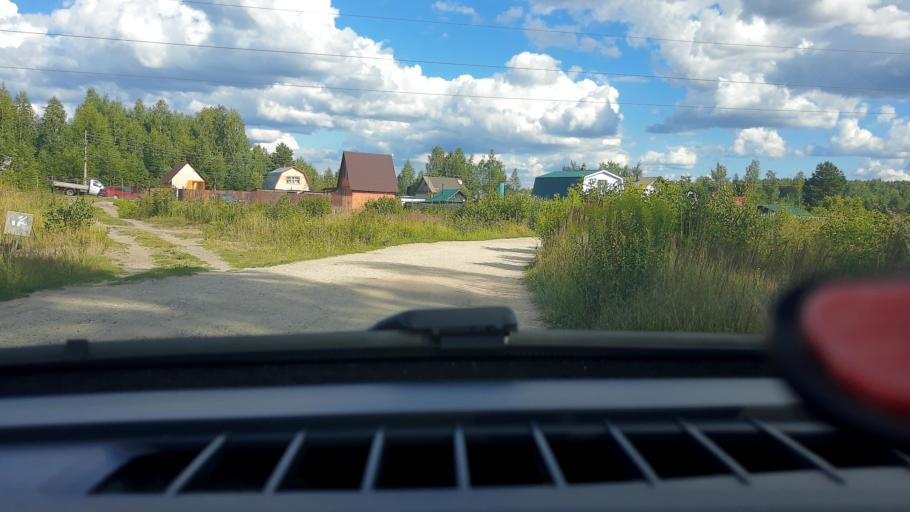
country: RU
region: Nizjnij Novgorod
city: Gorbatovka
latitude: 56.3355
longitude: 43.6659
